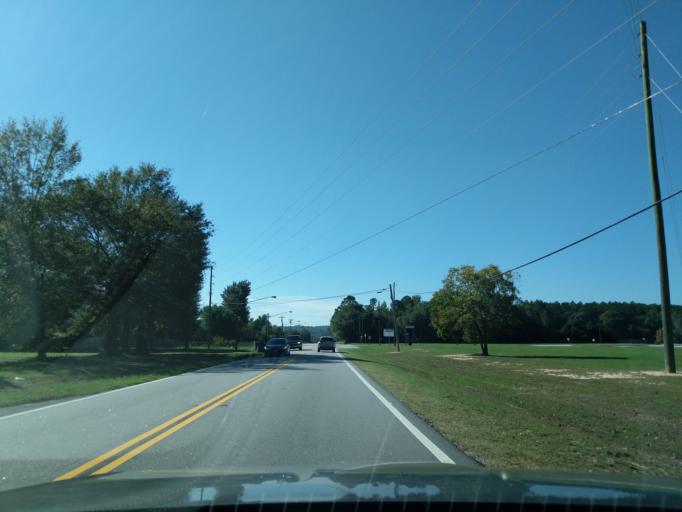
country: US
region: Georgia
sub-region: Richmond County
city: Hephzibah
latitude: 33.3556
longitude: -81.9987
